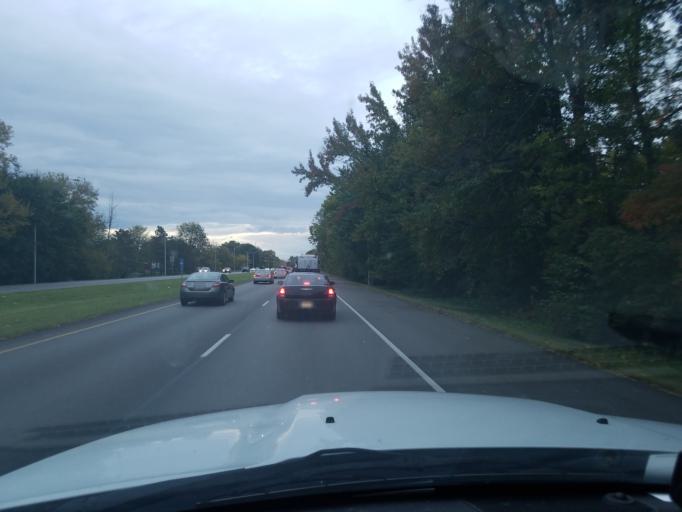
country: US
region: Indiana
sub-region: Vanderburgh County
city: Evansville
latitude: 37.9660
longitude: -87.5430
